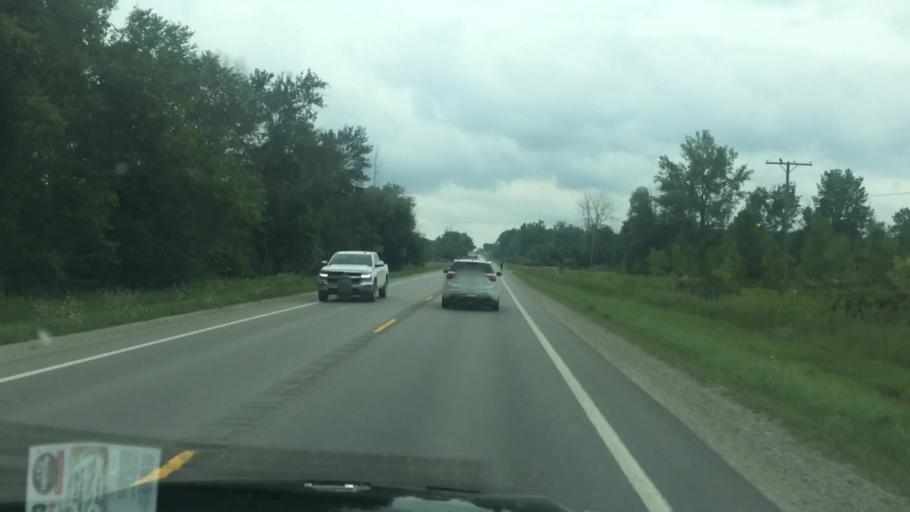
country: US
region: Michigan
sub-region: Tuscola County
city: Cass City
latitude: 43.5871
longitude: -83.0967
